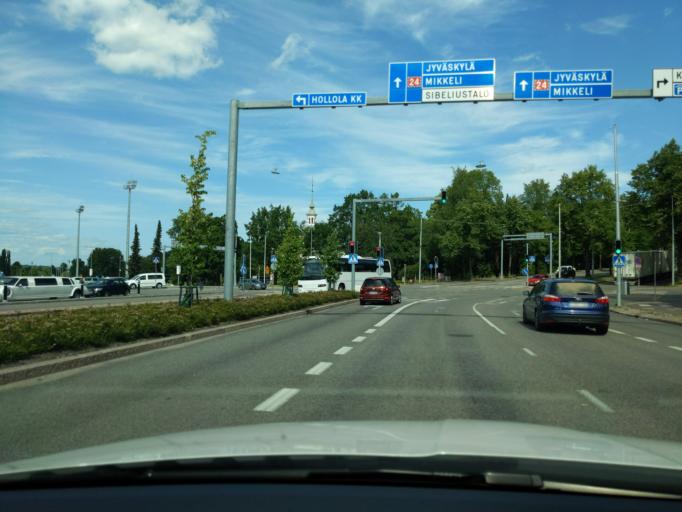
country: FI
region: Paijanne Tavastia
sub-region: Lahti
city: Lahti
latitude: 60.9842
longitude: 25.6514
